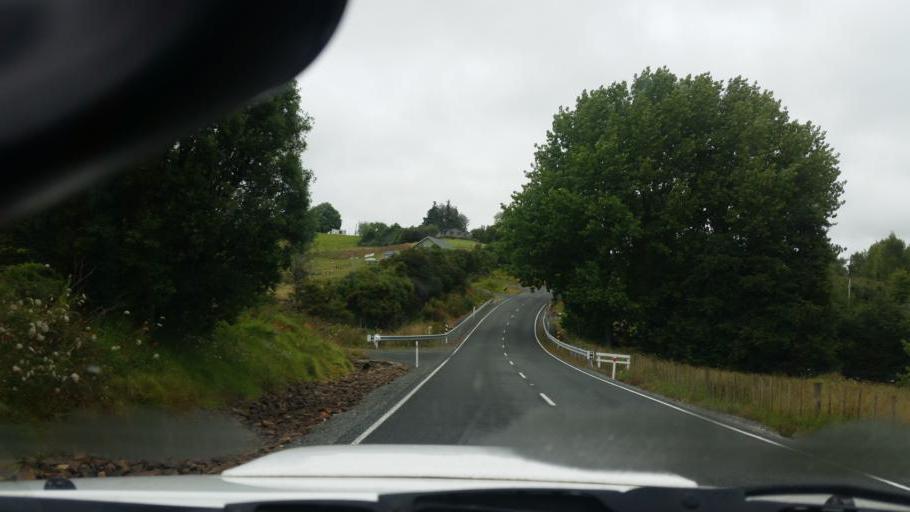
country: NZ
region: Auckland
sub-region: Auckland
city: Wellsford
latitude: -36.1708
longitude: 174.4611
